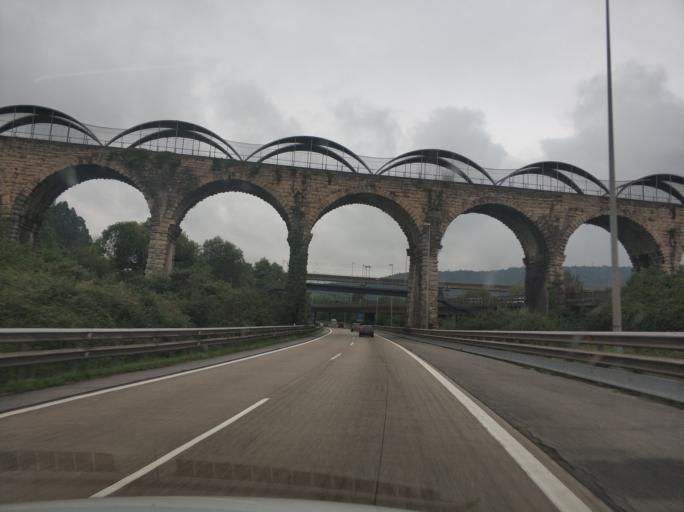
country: ES
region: Asturias
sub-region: Province of Asturias
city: Corvera de Asturias
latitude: 43.5009
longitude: -5.7869
